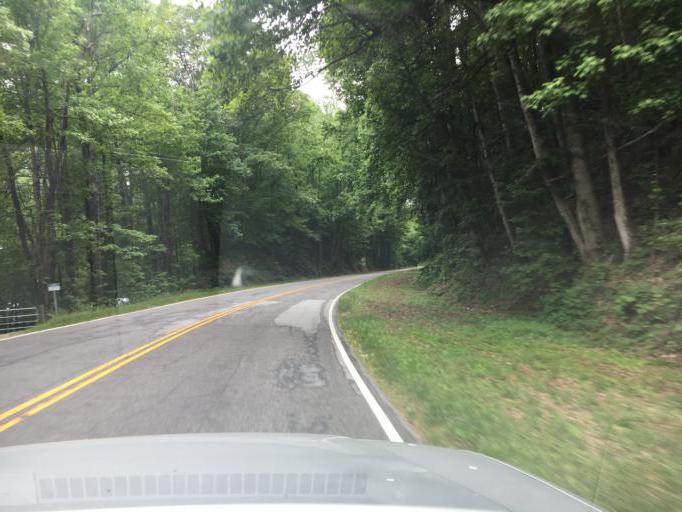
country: US
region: South Carolina
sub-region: Greenville County
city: Tigerville
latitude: 35.1526
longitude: -82.4181
